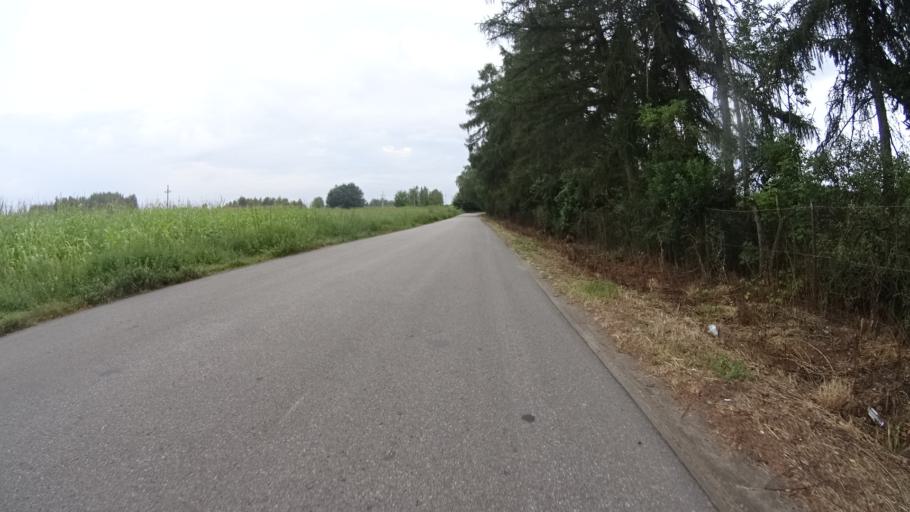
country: PL
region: Masovian Voivodeship
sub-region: Powiat grojecki
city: Goszczyn
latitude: 51.6866
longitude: 20.8609
